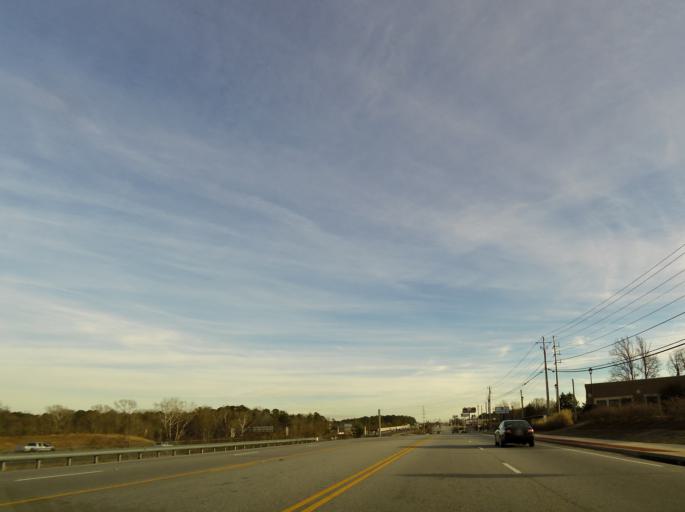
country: US
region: Georgia
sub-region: Bibb County
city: Macon
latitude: 32.8974
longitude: -83.6829
